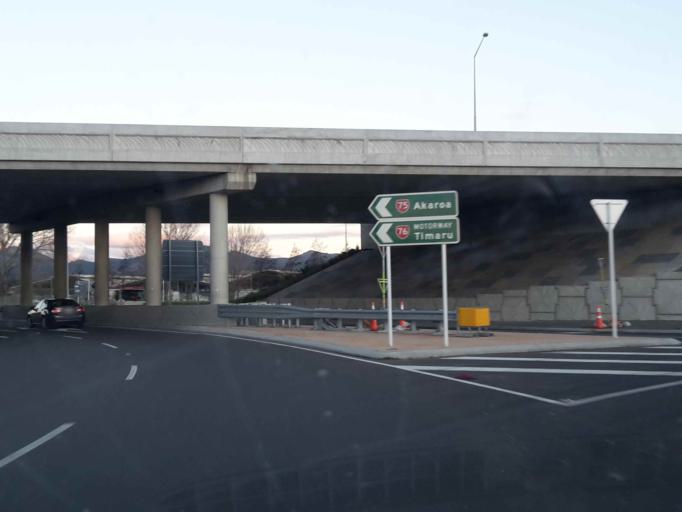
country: NZ
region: Canterbury
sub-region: Christchurch City
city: Christchurch
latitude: -43.5477
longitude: 172.5781
